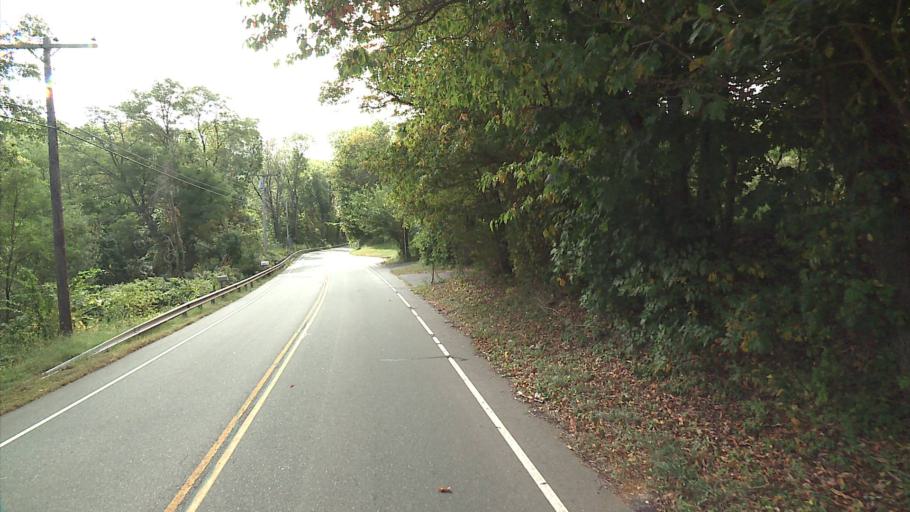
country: US
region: Connecticut
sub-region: Middlesex County
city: Durham
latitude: 41.5242
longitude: -72.7049
